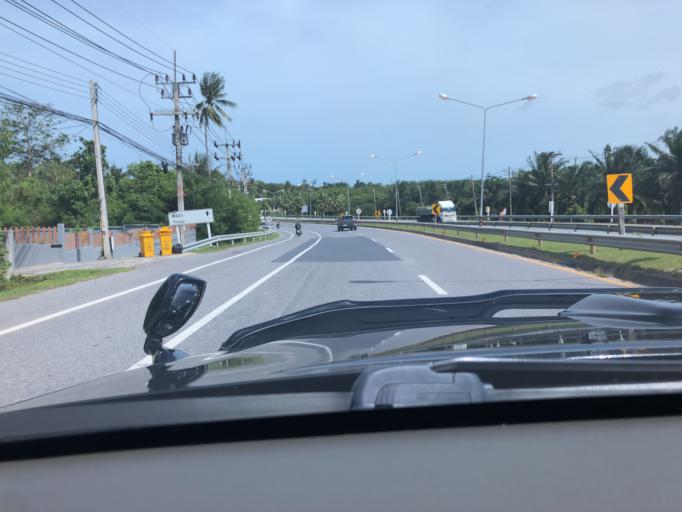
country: TH
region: Phuket
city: Thalang
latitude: 8.1566
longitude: 98.3225
